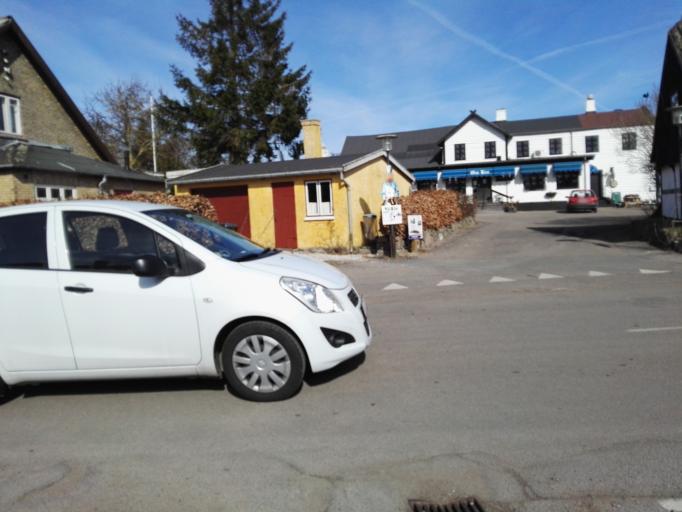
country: DK
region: Zealand
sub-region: Lejre Kommune
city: Ejby
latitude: 55.7667
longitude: 11.8076
